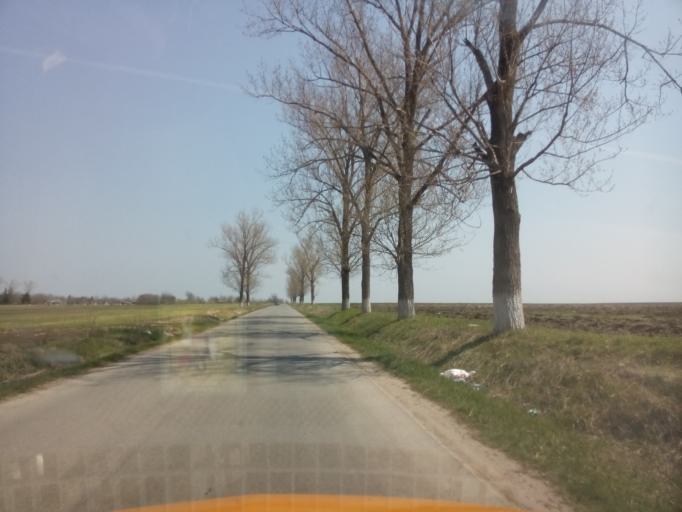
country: RO
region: Calarasi
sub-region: Comuna Luica
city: Luica
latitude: 44.2421
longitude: 26.6092
